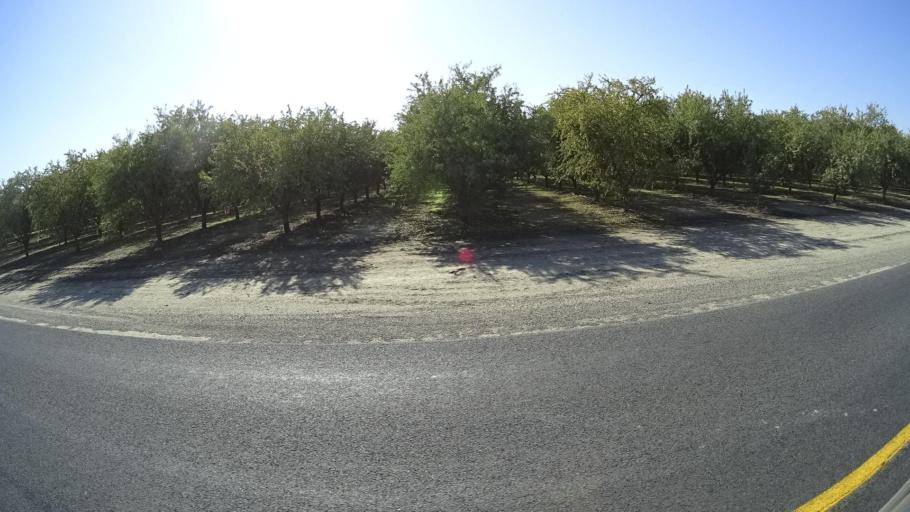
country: US
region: California
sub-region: Kern County
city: Wasco
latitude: 35.7176
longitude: -119.3756
